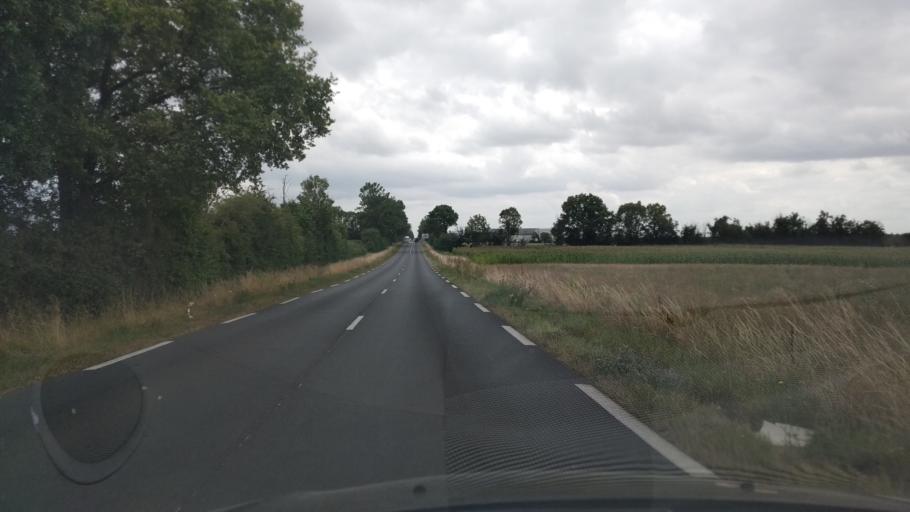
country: FR
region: Poitou-Charentes
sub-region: Departement de la Vienne
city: Roches-Premarie-Andille
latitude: 46.4992
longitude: 0.3643
